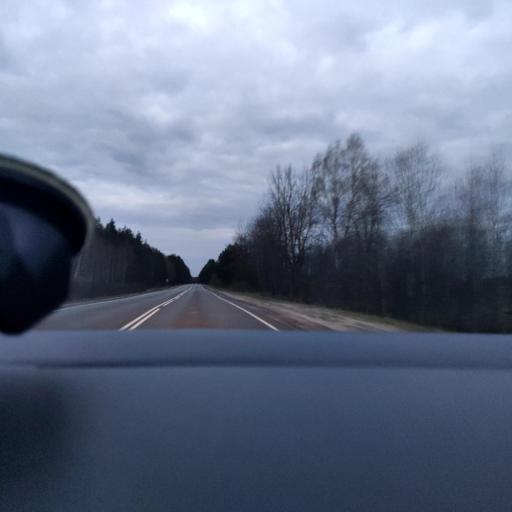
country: RU
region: Moskovskaya
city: Krasnyy Tkach
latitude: 55.4206
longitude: 39.1839
